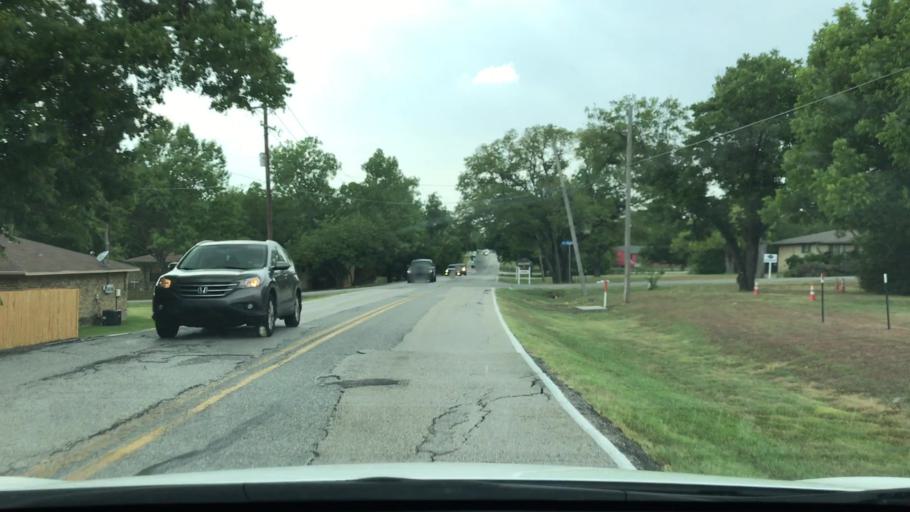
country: US
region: Texas
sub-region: Dallas County
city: Sachse
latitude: 32.9736
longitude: -96.5934
